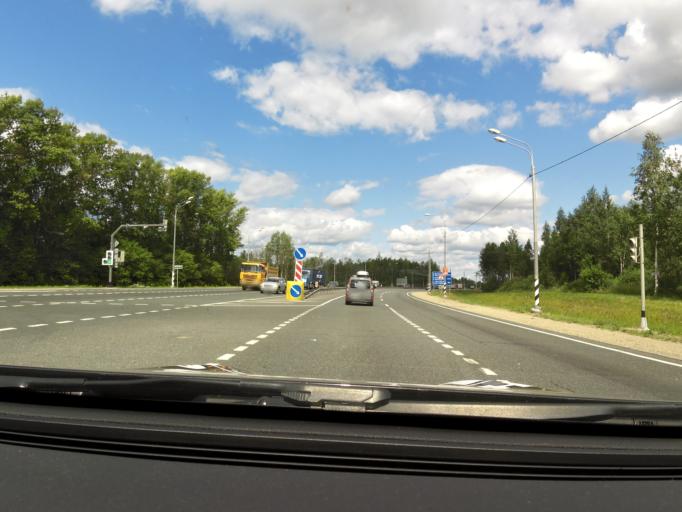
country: RU
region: Tverskaya
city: Torzhok
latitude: 57.0239
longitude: 35.0352
